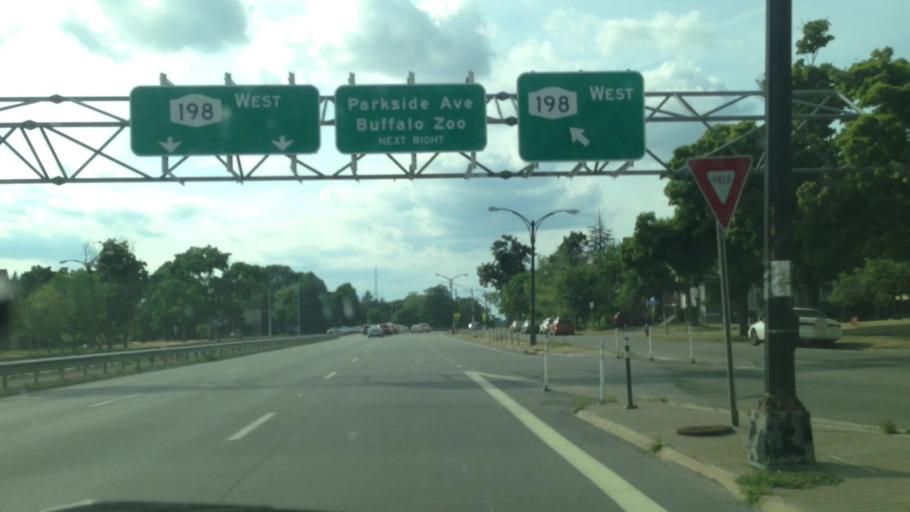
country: US
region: New York
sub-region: Erie County
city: Kenmore
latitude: 42.9291
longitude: -78.8528
